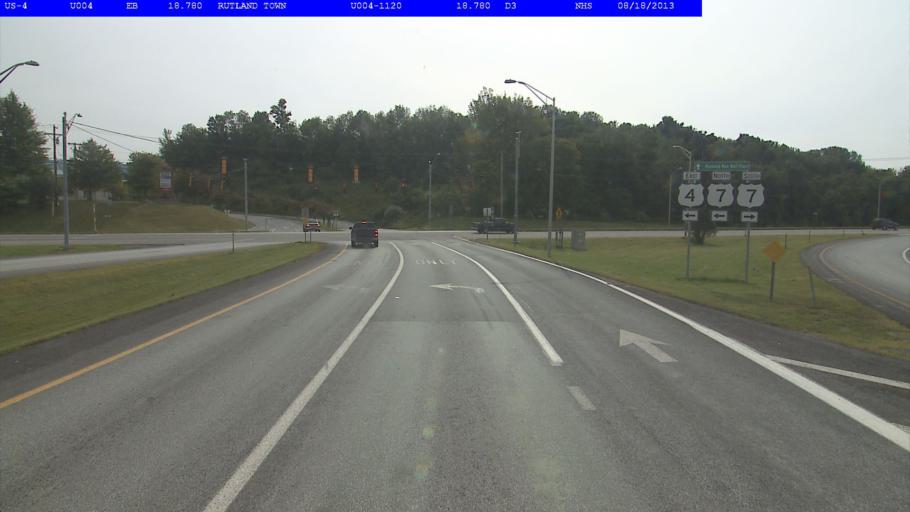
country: US
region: Vermont
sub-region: Rutland County
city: Rutland
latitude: 43.5786
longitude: -72.9676
